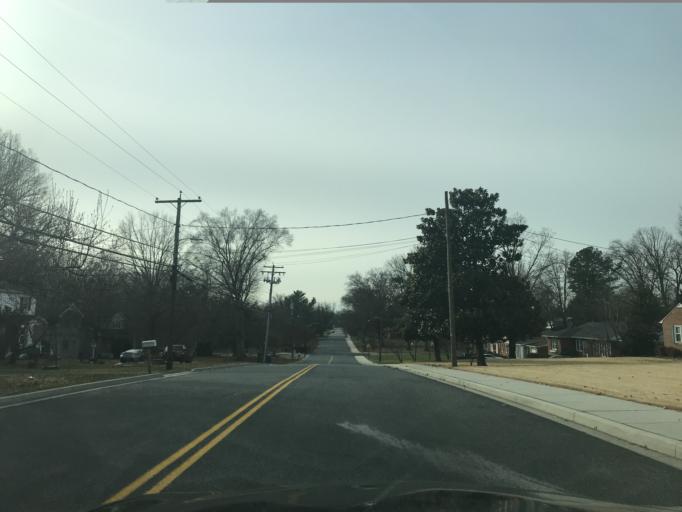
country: US
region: Maryland
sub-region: Harford County
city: Aberdeen
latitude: 39.5162
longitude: -76.1665
